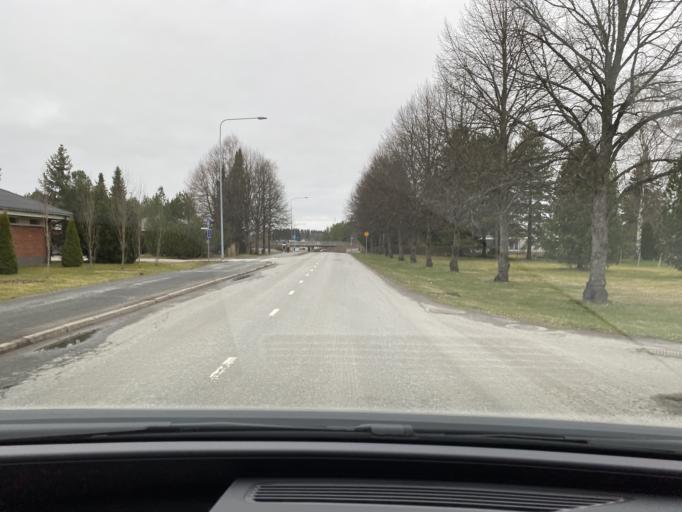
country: FI
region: Satakunta
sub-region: Pori
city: Huittinen
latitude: 61.1817
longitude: 22.6868
